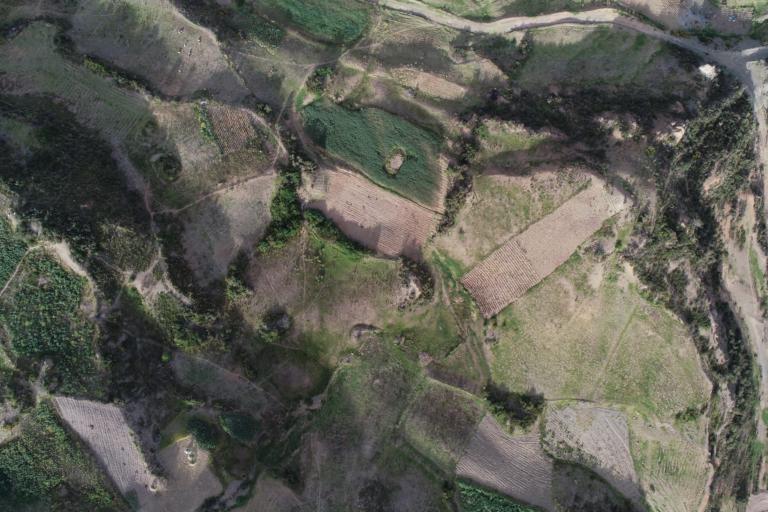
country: BO
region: La Paz
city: La Paz
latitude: -16.5490
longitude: -67.9986
